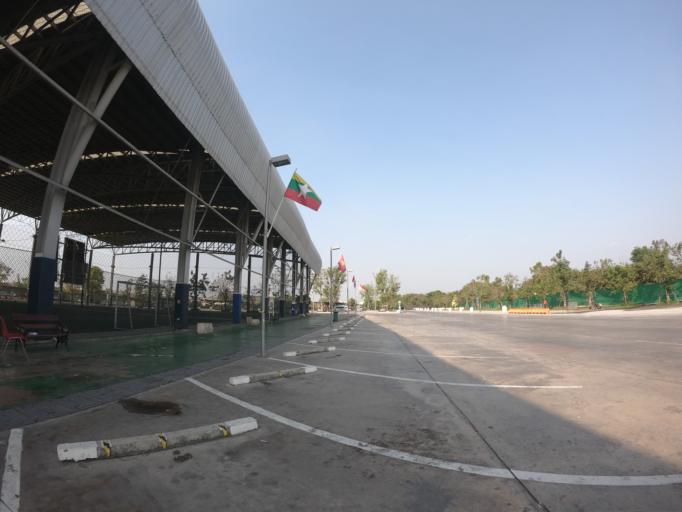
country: TH
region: Phra Nakhon Si Ayutthaya
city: Phra Nakhon Si Ayutthaya
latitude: 14.3381
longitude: 100.6089
